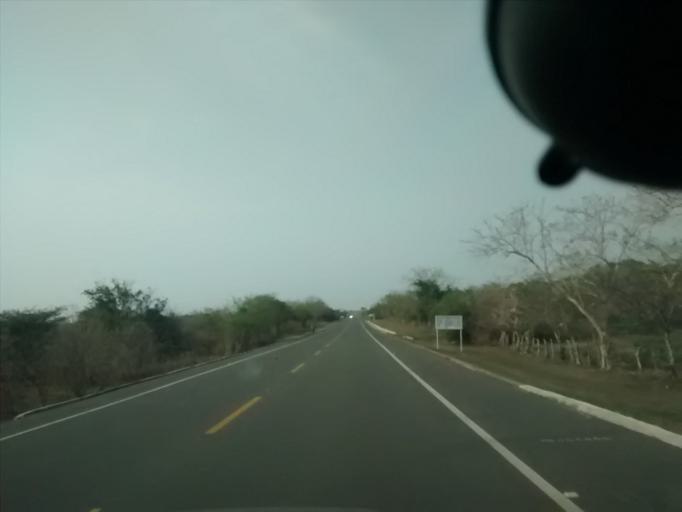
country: CO
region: Atlantico
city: Piojo
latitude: 10.7463
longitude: -75.2518
